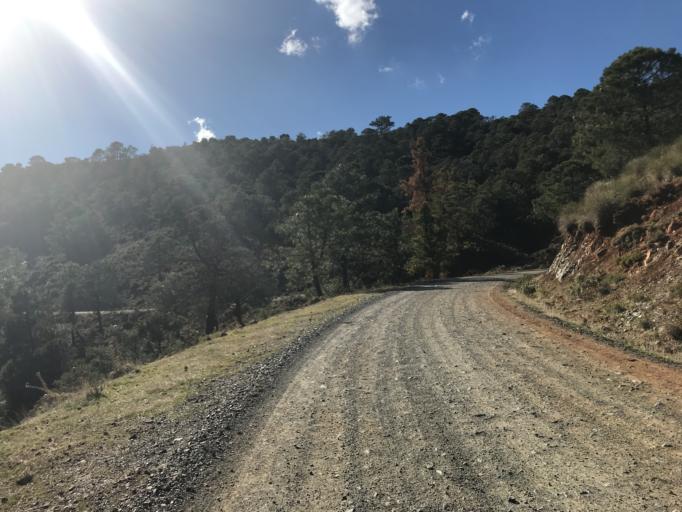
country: ES
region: Andalusia
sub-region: Provincia de Malaga
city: Tolox
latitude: 36.6793
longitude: -4.9255
